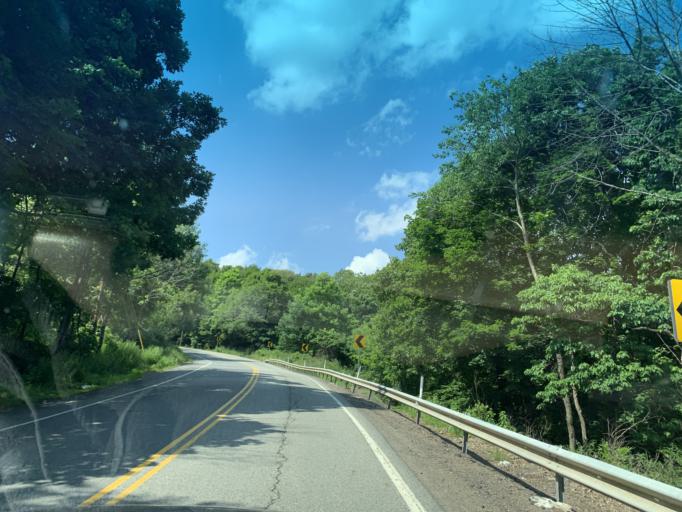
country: US
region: Pennsylvania
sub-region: Schuylkill County
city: Ashland
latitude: 40.7981
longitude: -76.3381
